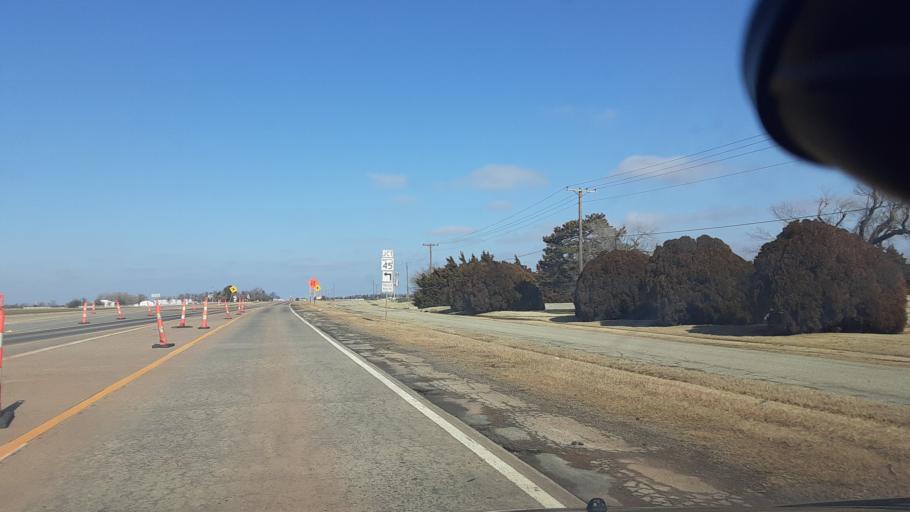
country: US
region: Oklahoma
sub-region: Garfield County
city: Enid
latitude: 36.4588
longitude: -97.8729
